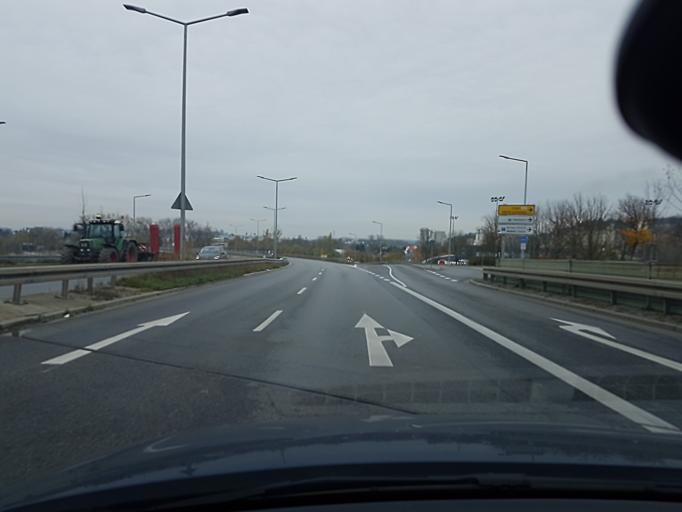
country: DE
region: Bavaria
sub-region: Upper Palatinate
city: Regensburg
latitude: 49.0240
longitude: 12.1398
